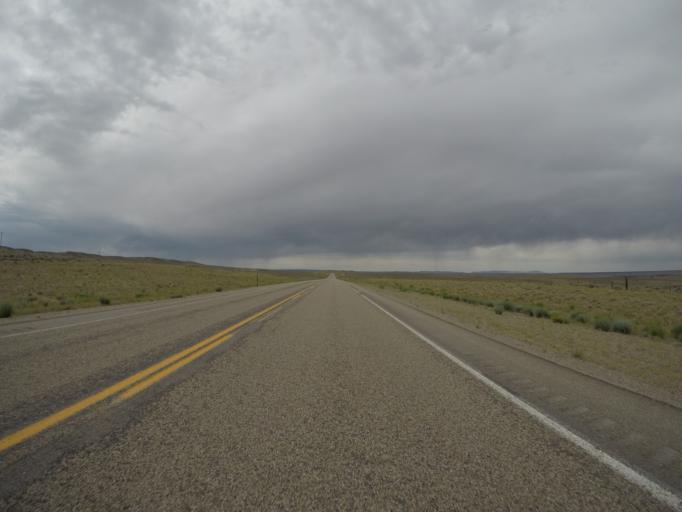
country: US
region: Wyoming
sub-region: Lincoln County
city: Kemmerer
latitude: 41.9556
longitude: -110.0379
